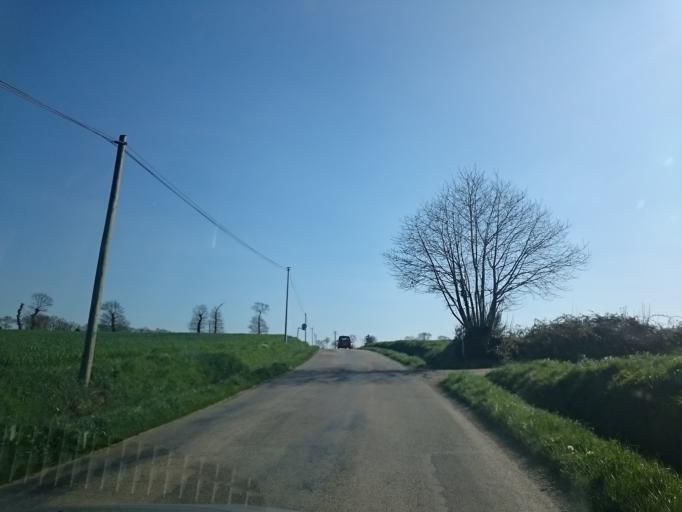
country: FR
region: Brittany
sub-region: Departement d'Ille-et-Vilaine
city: Orgeres
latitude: 47.9879
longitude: -1.6734
